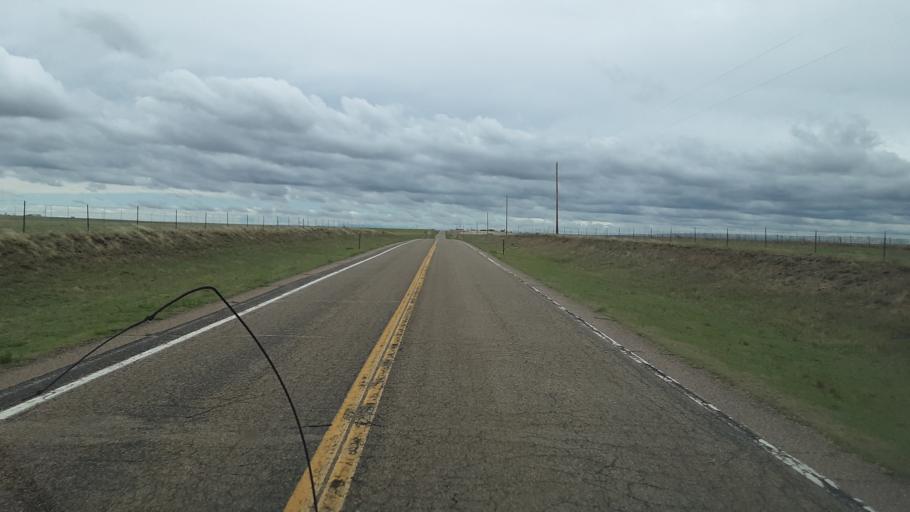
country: US
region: Colorado
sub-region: Lincoln County
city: Limon
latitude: 38.8383
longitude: -103.8609
